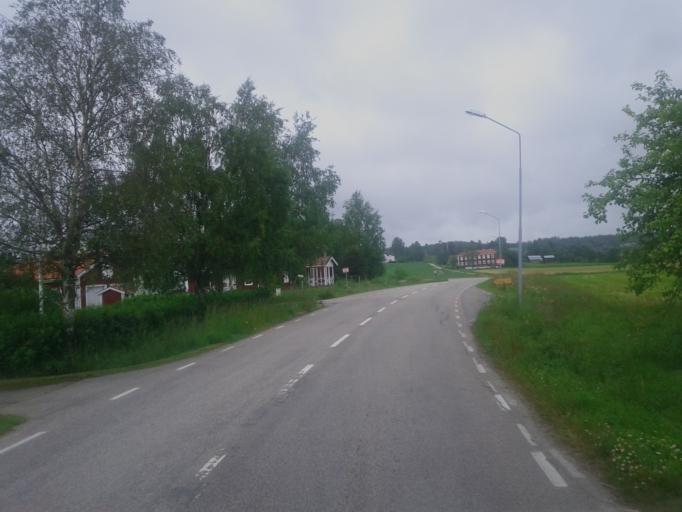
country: SE
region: Gaevleborg
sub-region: Nordanstigs Kommun
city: Bergsjoe
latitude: 61.9745
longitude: 17.2520
